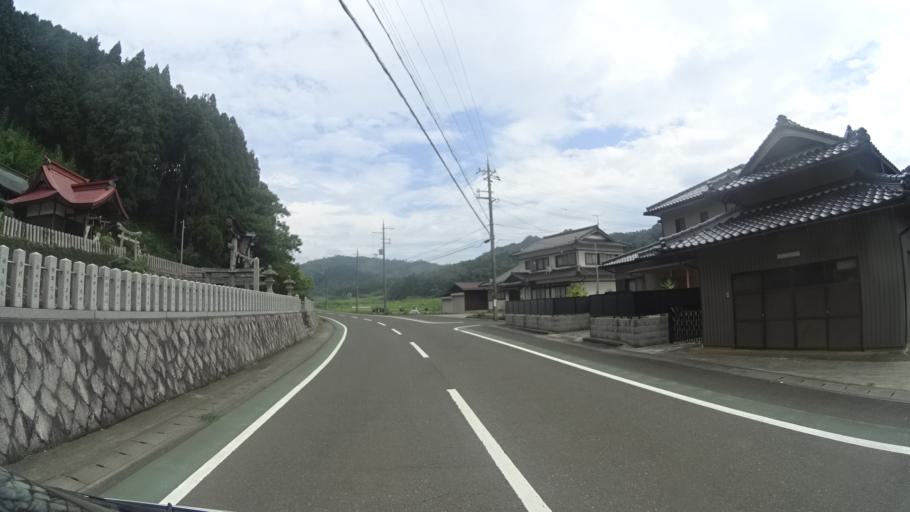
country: JP
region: Kyoto
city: Ayabe
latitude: 35.3578
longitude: 135.3221
